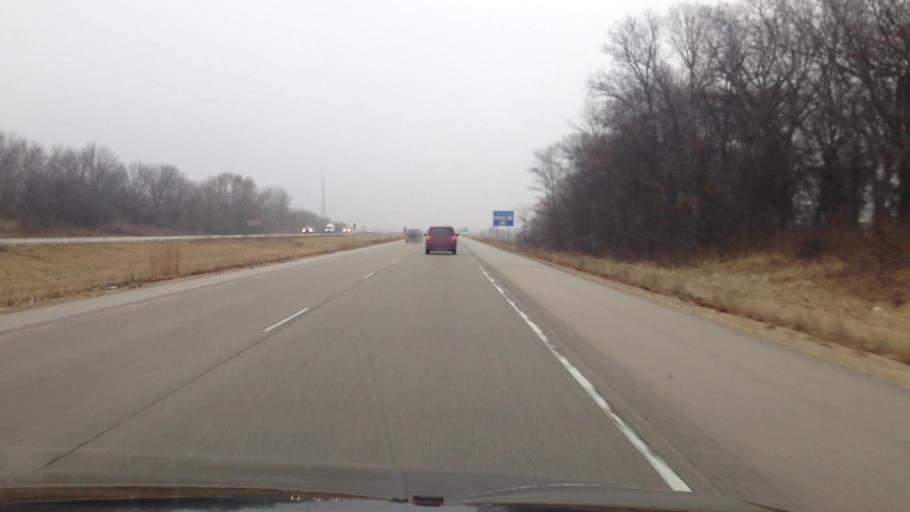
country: US
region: Wisconsin
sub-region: Waukesha County
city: Mukwonago
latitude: 42.8433
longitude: -88.3325
